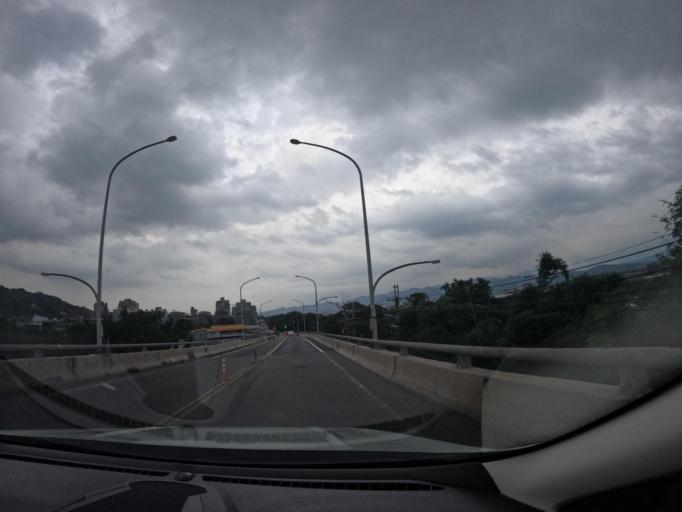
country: TW
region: Taiwan
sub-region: Taoyuan
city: Taoyuan
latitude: 24.9683
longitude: 121.3877
